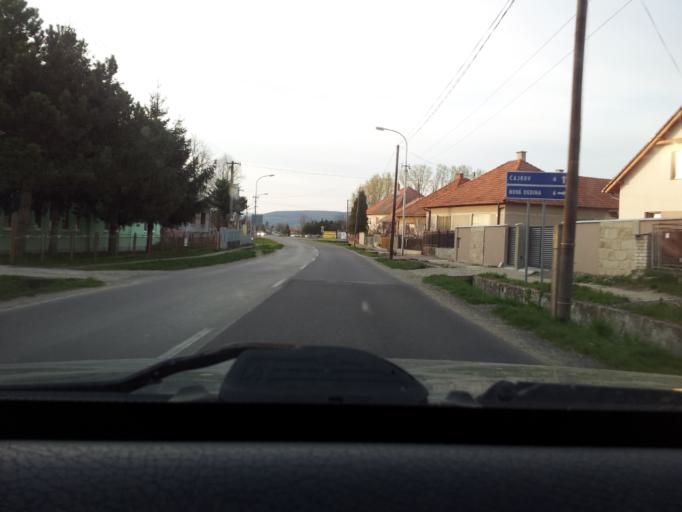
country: SK
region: Nitriansky
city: Levice
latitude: 48.2575
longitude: 18.6046
